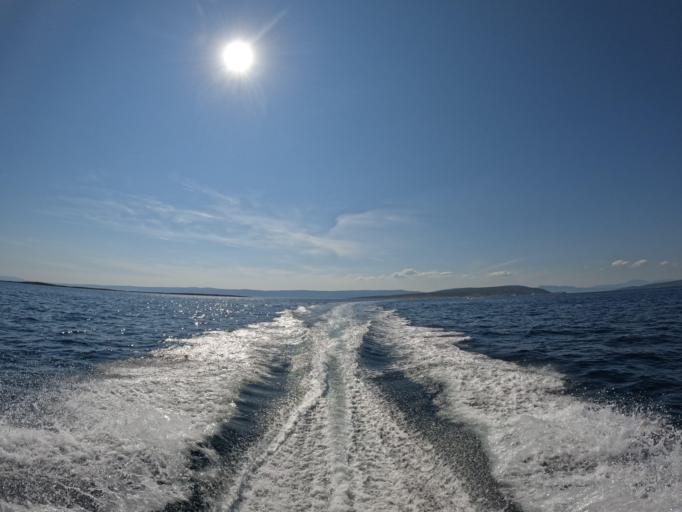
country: HR
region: Primorsko-Goranska
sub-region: Grad Krk
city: Krk
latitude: 44.9540
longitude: 14.5844
